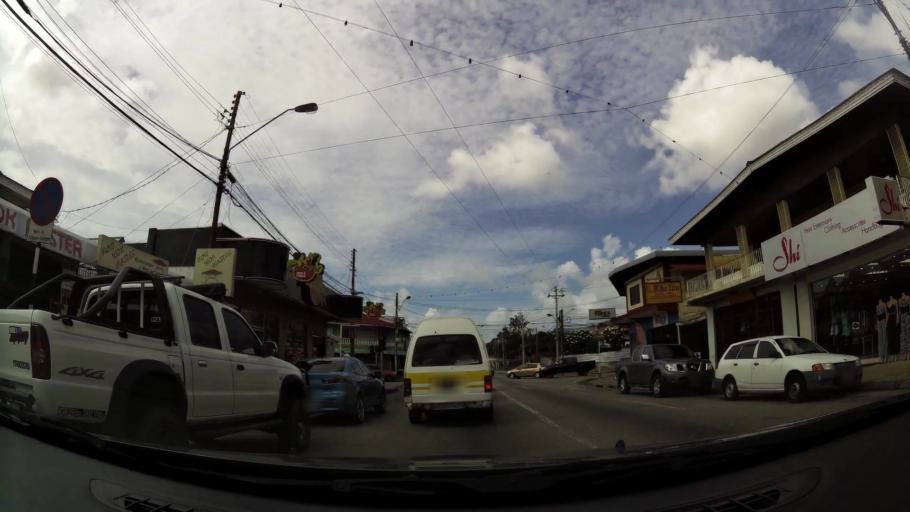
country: TT
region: City of Port of Spain
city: Mucurapo
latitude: 10.6730
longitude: -61.5375
